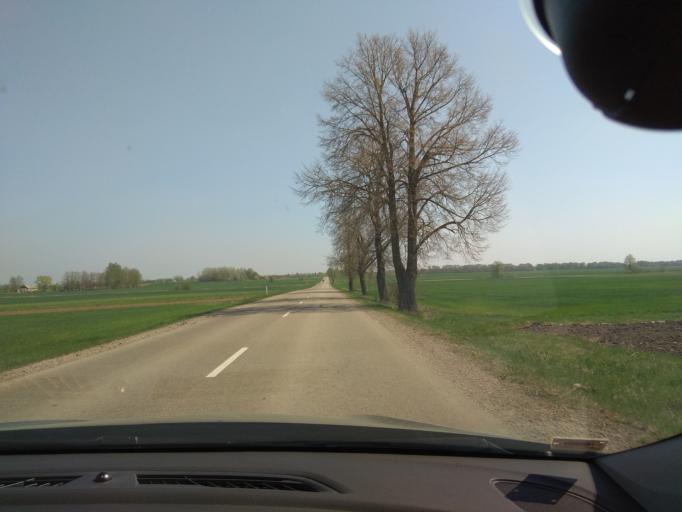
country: LT
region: Panevezys
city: Pasvalys
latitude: 55.9427
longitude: 24.2174
